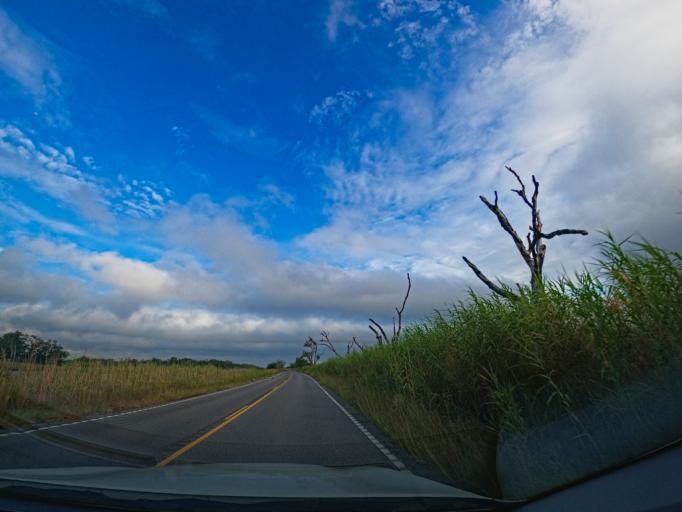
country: US
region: Louisiana
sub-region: Terrebonne Parish
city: Dulac
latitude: 29.3406
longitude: -90.6937
